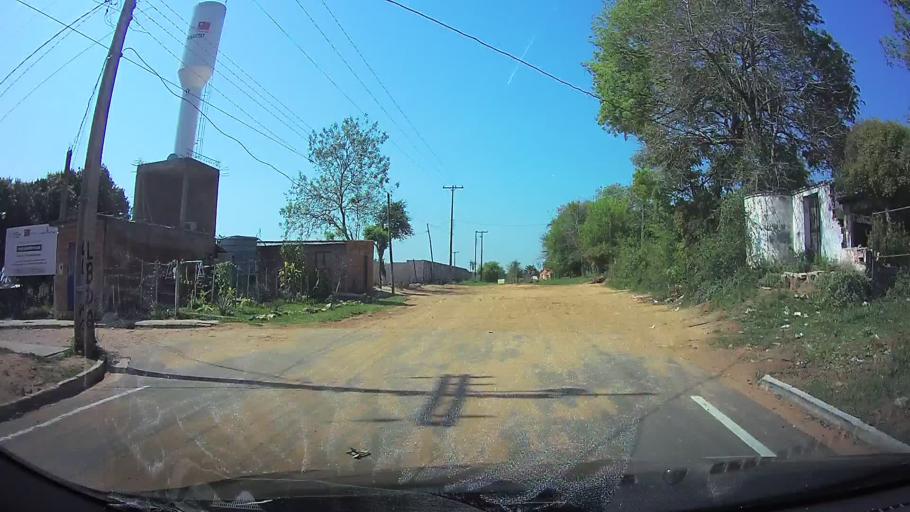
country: PY
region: Central
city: Limpio
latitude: -25.2190
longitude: -57.4847
